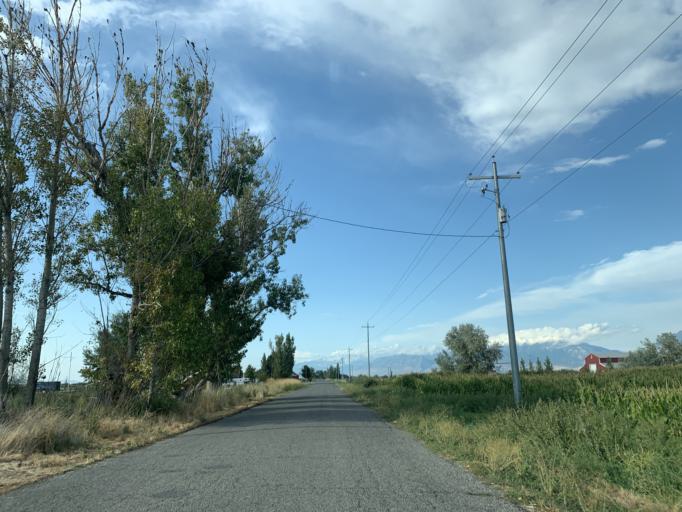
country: US
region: Utah
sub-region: Utah County
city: Benjamin
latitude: 40.1246
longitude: -111.7691
